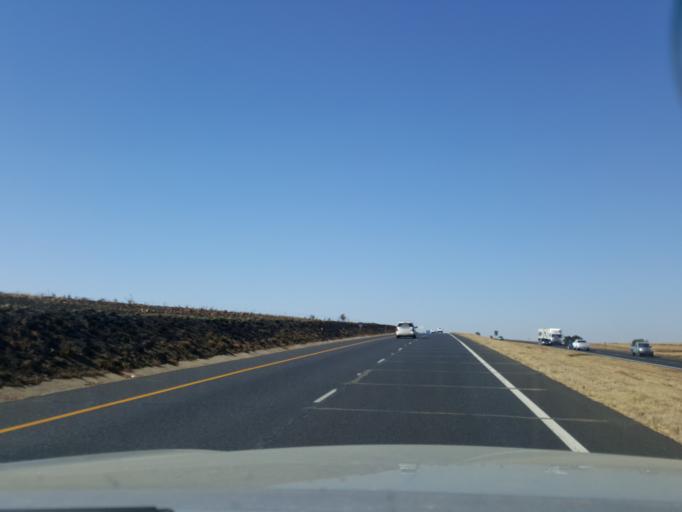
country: ZA
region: Mpumalanga
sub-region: Nkangala District Municipality
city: Witbank
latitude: -25.8777
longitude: 29.3278
